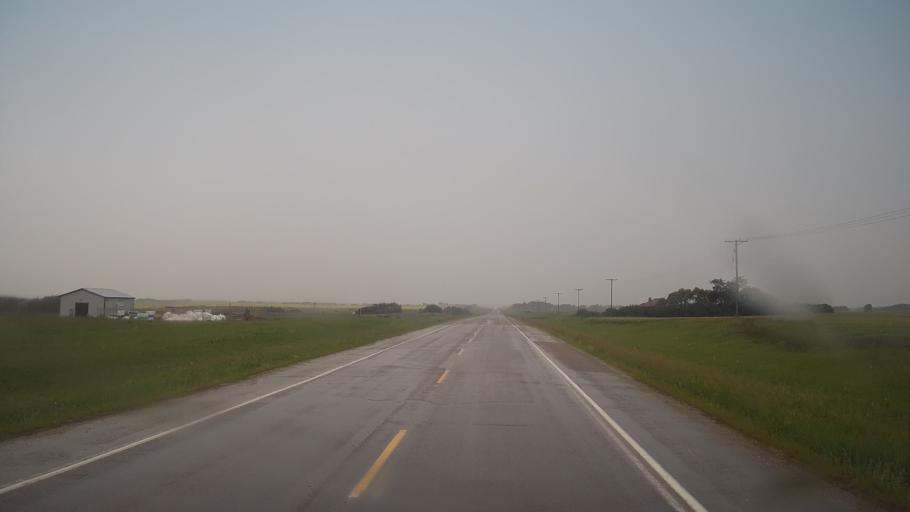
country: CA
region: Saskatchewan
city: Biggar
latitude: 52.1290
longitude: -108.1417
